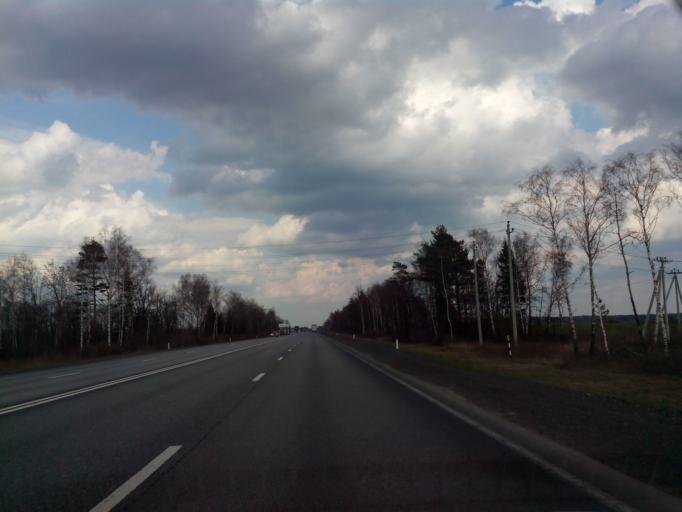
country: RU
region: Moskovskaya
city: Dorokhovo
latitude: 55.5051
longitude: 36.2254
